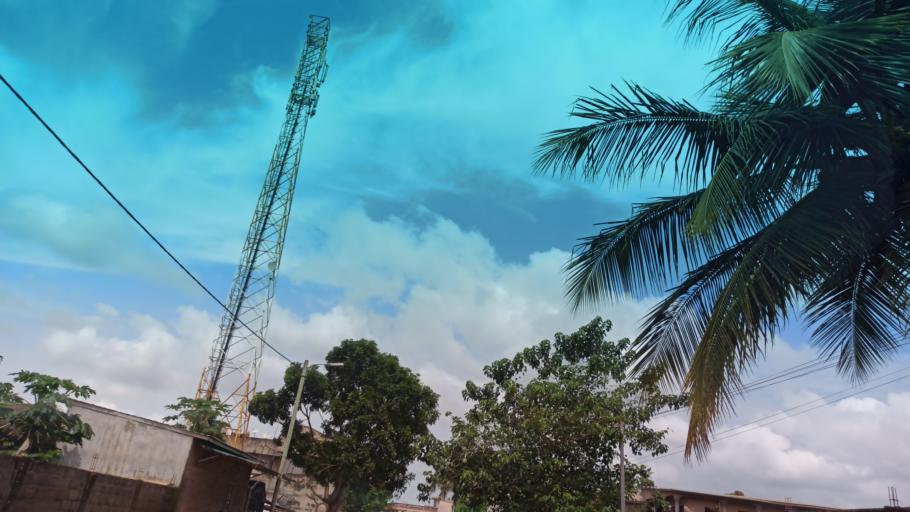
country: BJ
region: Queme
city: Porto-Novo
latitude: 6.4999
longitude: 2.5867
